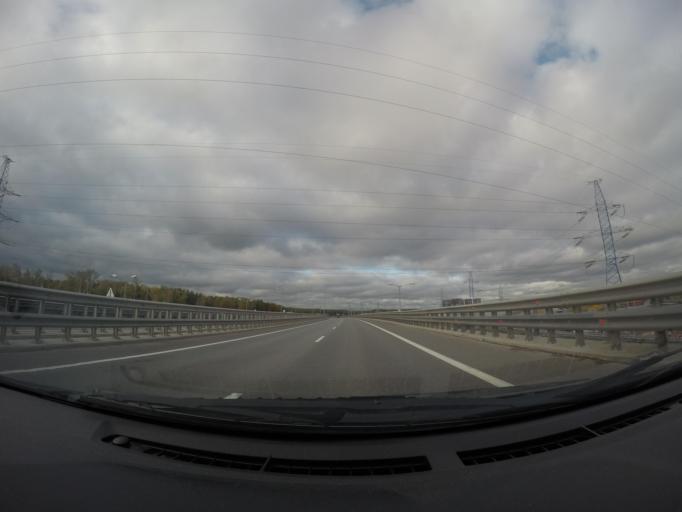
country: RU
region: Moskovskaya
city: Lesnoy Gorodok
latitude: 55.6650
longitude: 37.2247
